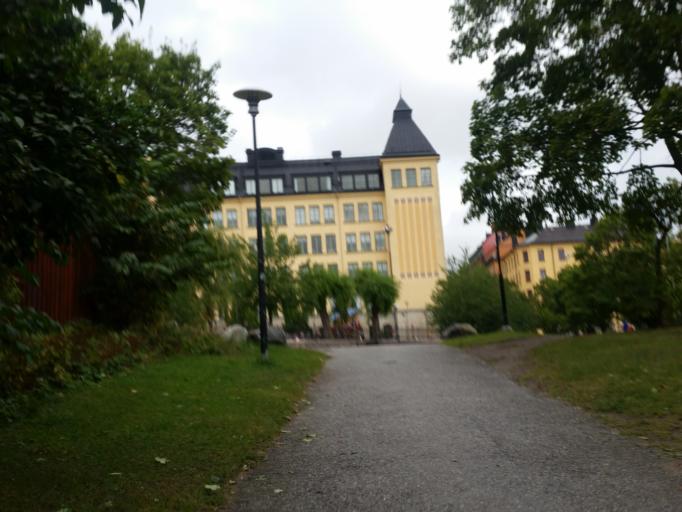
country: SE
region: Stockholm
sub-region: Stockholms Kommun
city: OEstermalm
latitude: 59.3121
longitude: 18.0934
